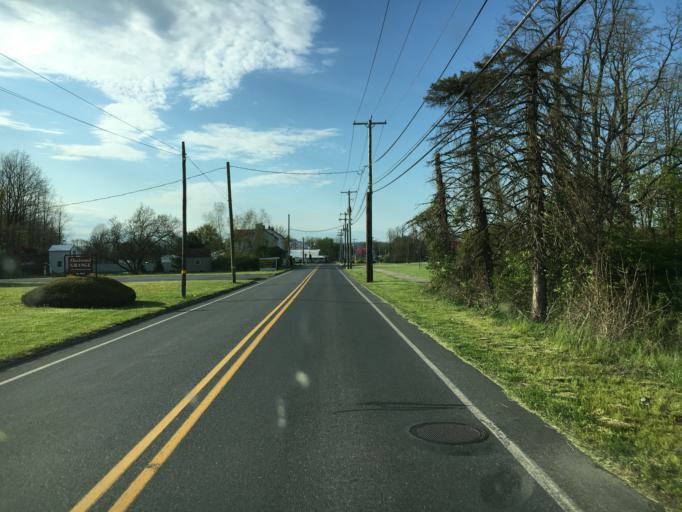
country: US
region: Pennsylvania
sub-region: Berks County
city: Fleetwood
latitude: 40.4602
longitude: -75.8201
